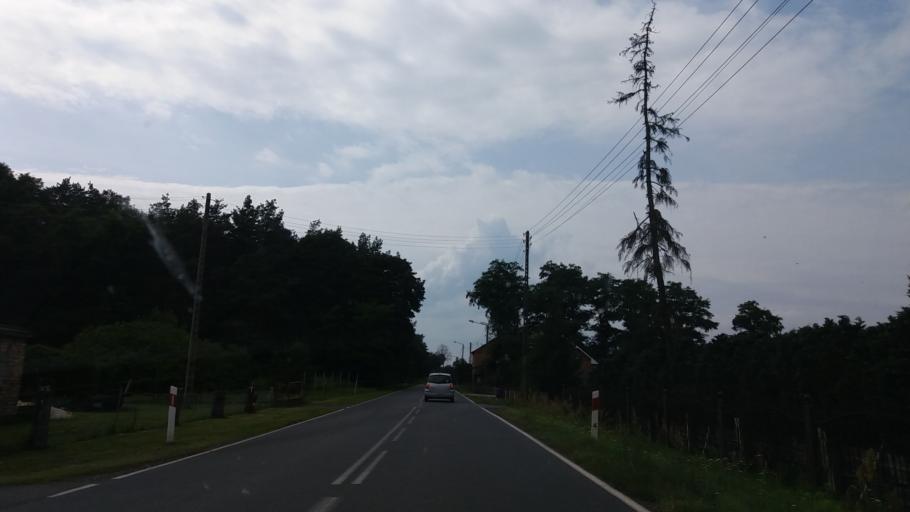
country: PL
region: Lubusz
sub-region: Powiat strzelecko-drezdenecki
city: Zwierzyn
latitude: 52.7249
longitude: 15.5702
